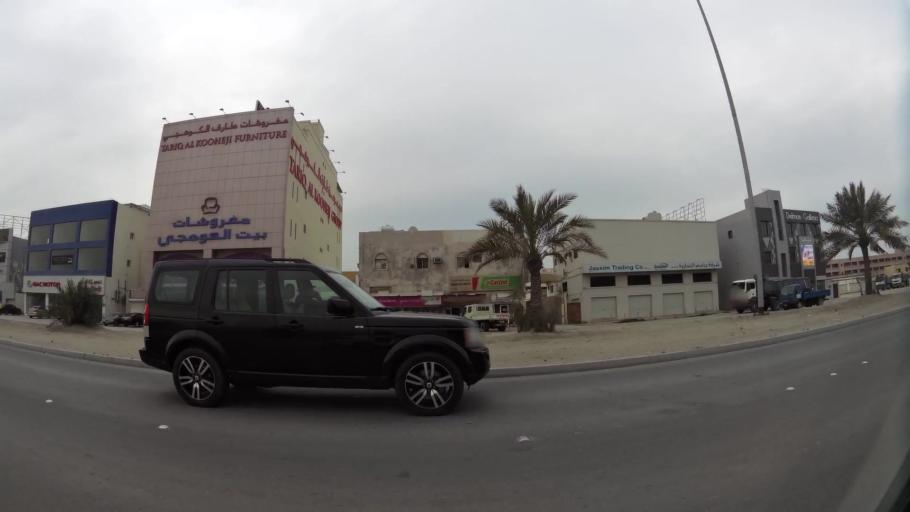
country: BH
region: Northern
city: Sitrah
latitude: 26.1393
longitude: 50.6119
